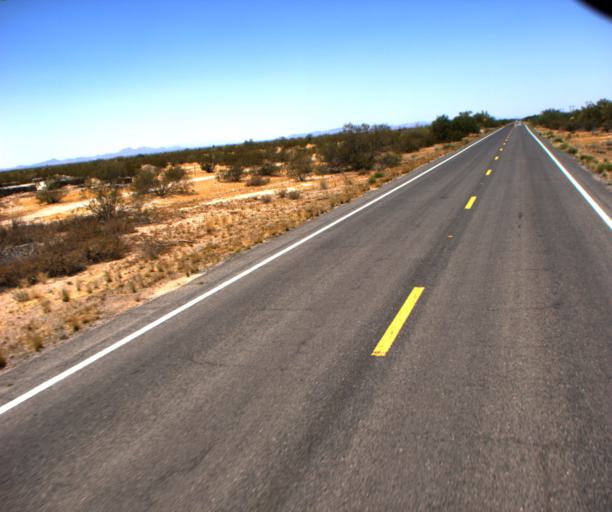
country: US
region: Arizona
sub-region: Pinal County
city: Florence
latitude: 32.9111
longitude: -111.2885
